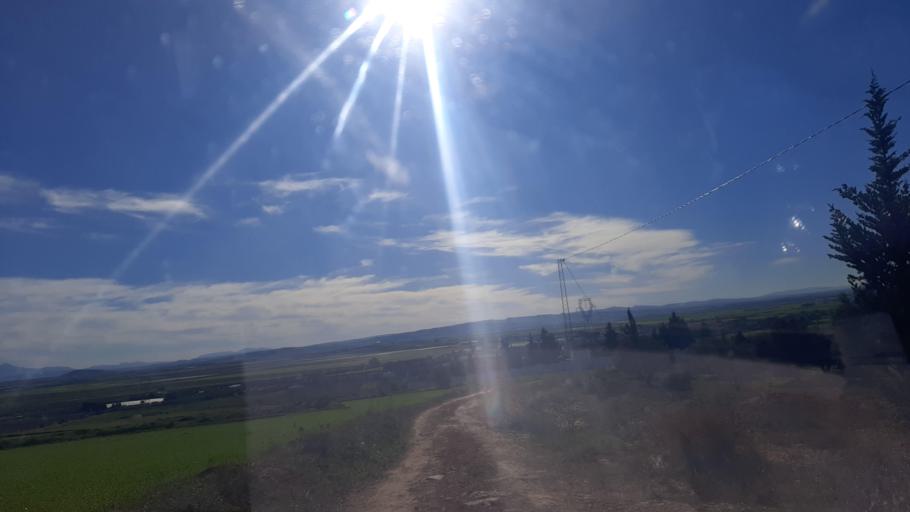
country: TN
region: Tunis
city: Oued Lill
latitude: 36.7646
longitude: 9.9856
